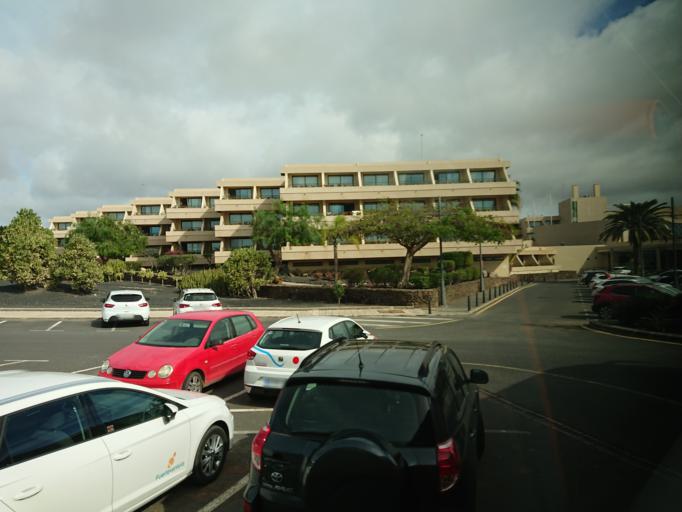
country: ES
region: Canary Islands
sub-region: Provincia de Las Palmas
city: Playa Blanca
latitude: 28.8634
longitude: -13.8214
